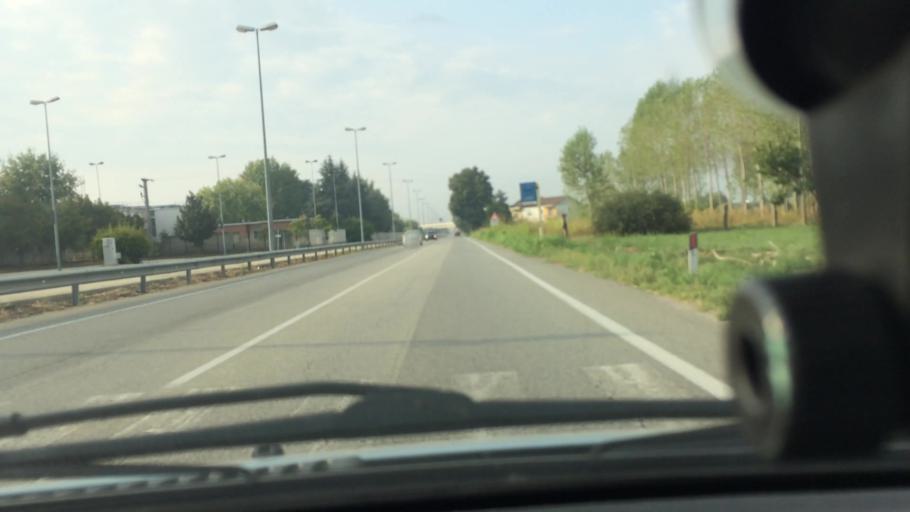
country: IT
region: Piedmont
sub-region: Provincia di Torino
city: Villastellone
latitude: 44.9130
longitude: 7.7433
